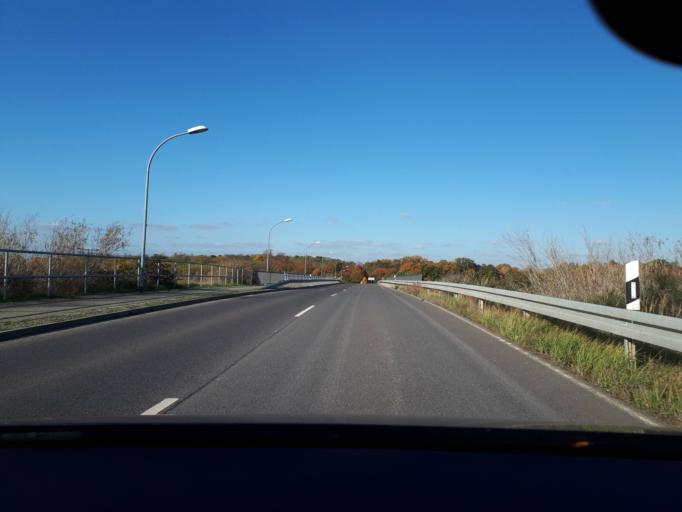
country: DE
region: Brandenburg
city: Schonefeld
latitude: 52.3703
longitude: 13.5403
